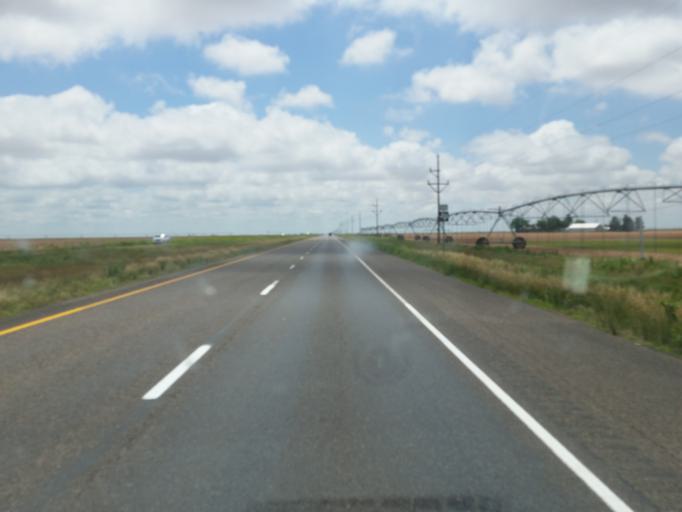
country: US
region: Texas
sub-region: Lubbock County
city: Slaton
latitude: 33.3952
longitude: -101.6060
